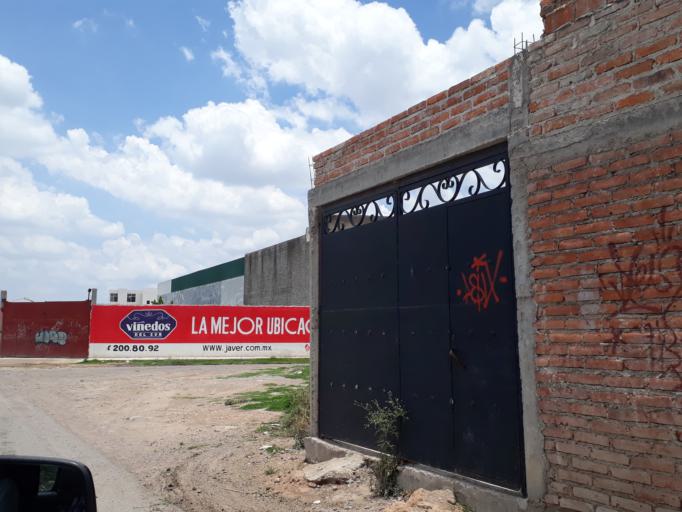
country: MX
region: Aguascalientes
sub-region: Aguascalientes
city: San Sebastian [Fraccionamiento]
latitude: 21.8029
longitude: -102.2764
